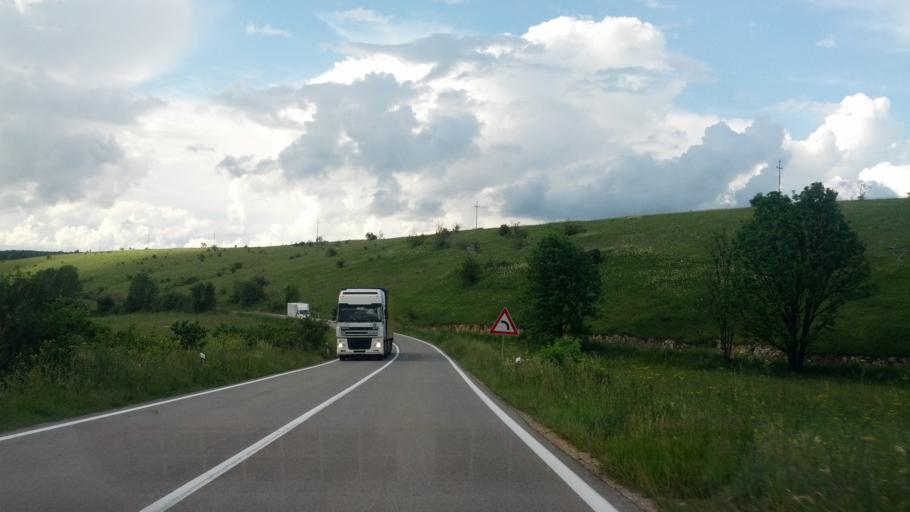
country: BA
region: Federation of Bosnia and Herzegovina
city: Izacic
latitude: 44.9127
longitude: 15.7188
